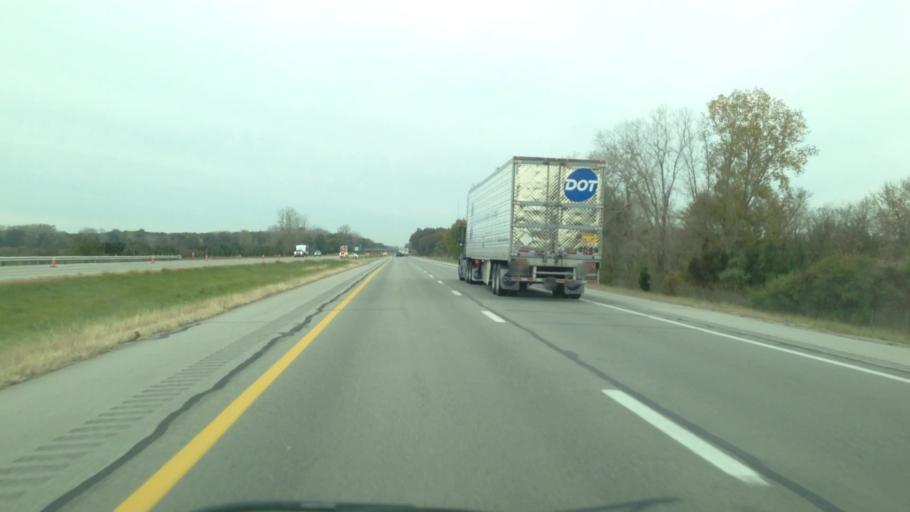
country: US
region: Ohio
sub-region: Lucas County
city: Holland
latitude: 41.5913
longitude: -83.7469
